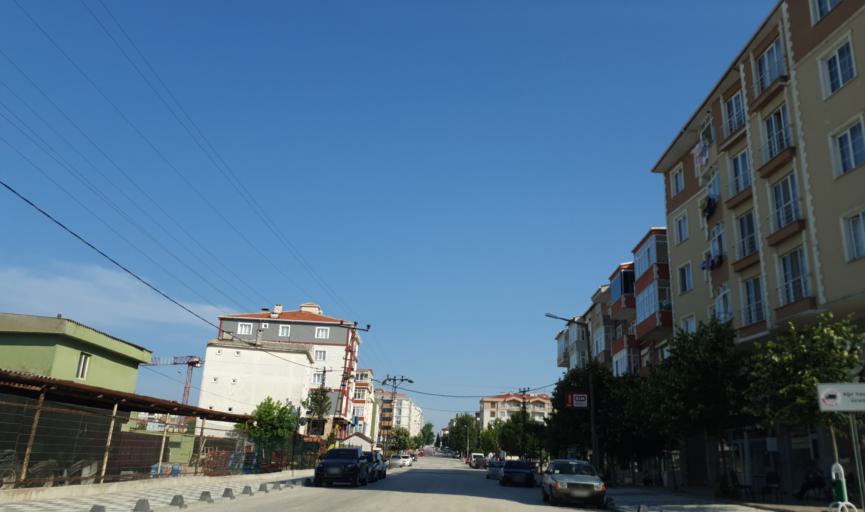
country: TR
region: Tekirdag
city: Saray
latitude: 41.4459
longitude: 27.9164
